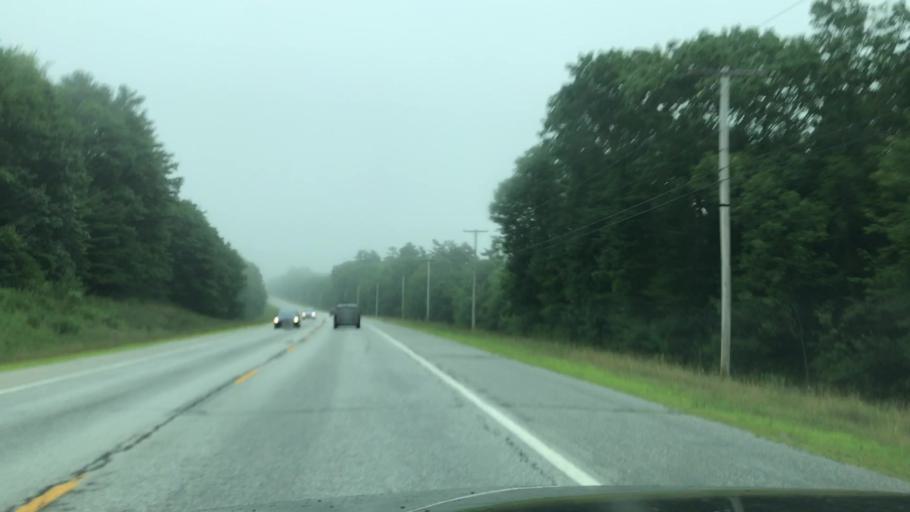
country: US
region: Maine
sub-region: Lincoln County
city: Nobleboro
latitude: 44.0775
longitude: -69.4771
